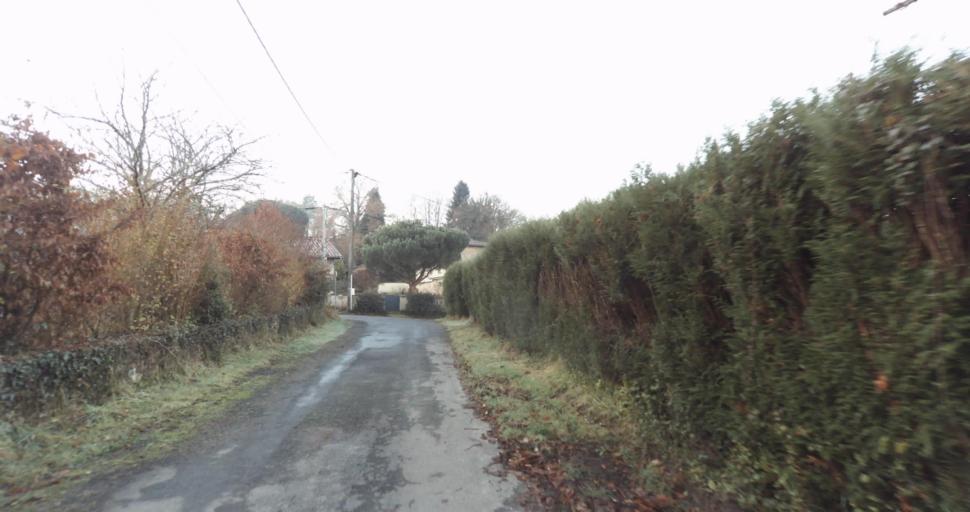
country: FR
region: Limousin
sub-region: Departement de la Haute-Vienne
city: Aixe-sur-Vienne
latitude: 45.8184
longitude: 1.1522
